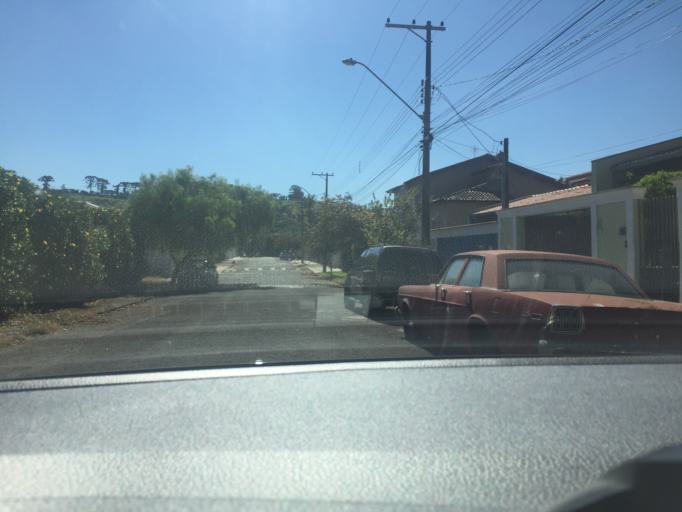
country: BR
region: Sao Paulo
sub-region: Santo Antonio Do Jardim
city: Espirito Santo do Pinhal
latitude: -22.1814
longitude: -46.7433
